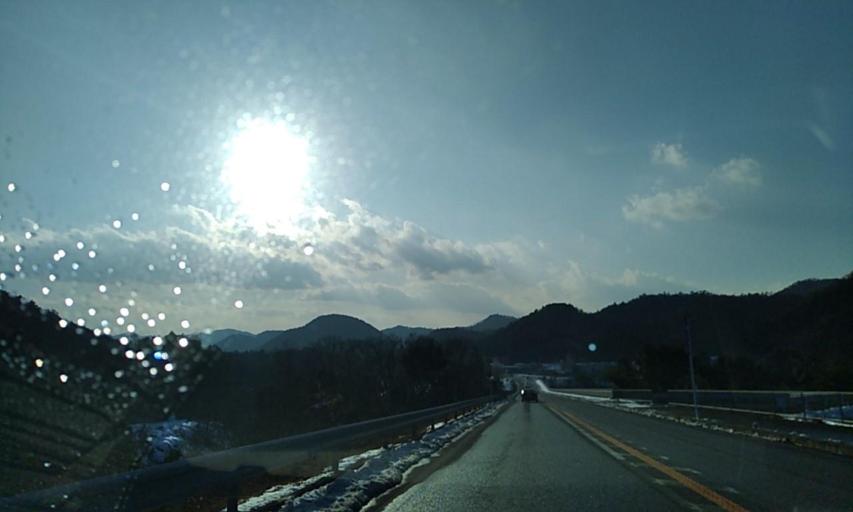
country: JP
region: Kyoto
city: Ayabe
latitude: 35.1995
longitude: 135.4263
